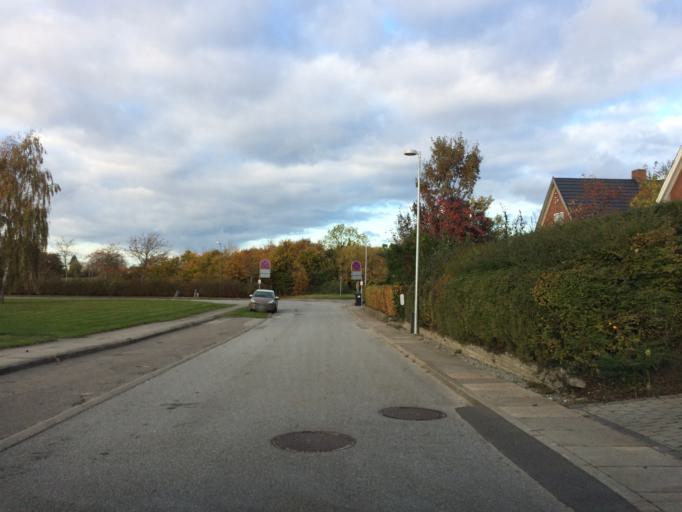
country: DK
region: South Denmark
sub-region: Sonderborg Kommune
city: Nordborg
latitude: 55.0397
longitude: 9.7949
